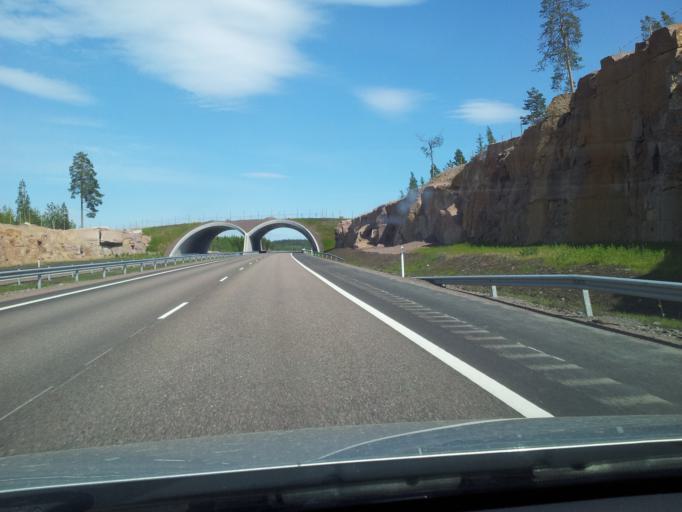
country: FI
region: Uusimaa
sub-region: Loviisa
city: Lovisa
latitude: 60.4898
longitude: 26.3238
